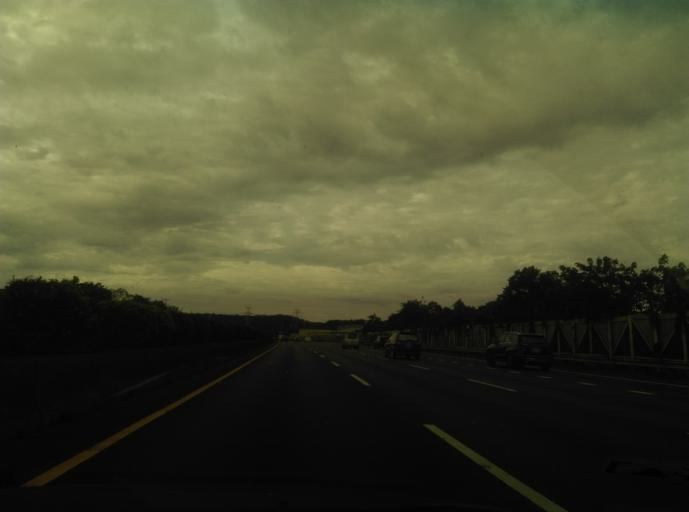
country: TW
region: Taiwan
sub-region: Taoyuan
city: Taoyuan
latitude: 24.9380
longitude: 121.3367
